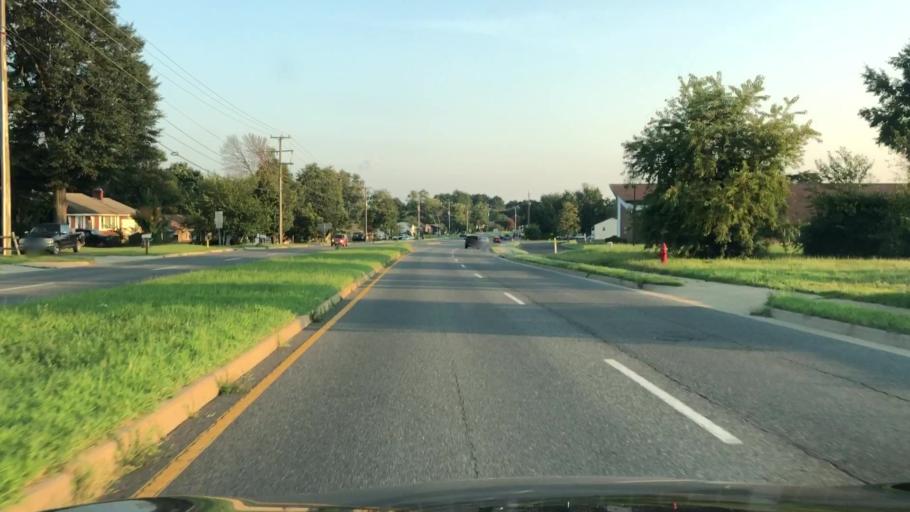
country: US
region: Virginia
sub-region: Stafford County
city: Falmouth
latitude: 38.3048
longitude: -77.5166
